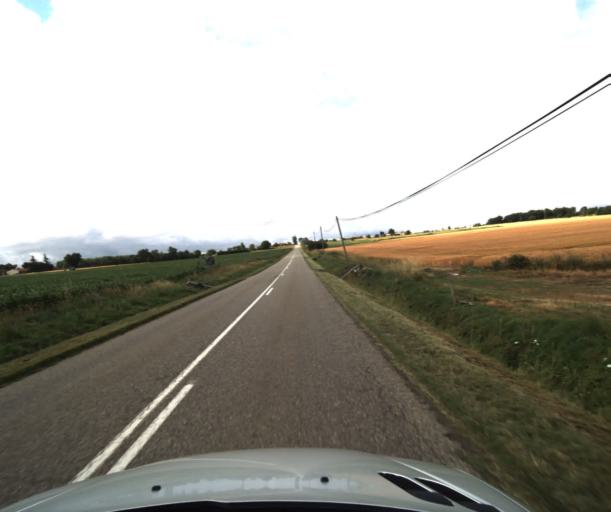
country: FR
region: Midi-Pyrenees
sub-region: Departement du Tarn-et-Garonne
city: Saint-Nicolas-de-la-Grave
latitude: 44.0054
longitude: 0.9908
